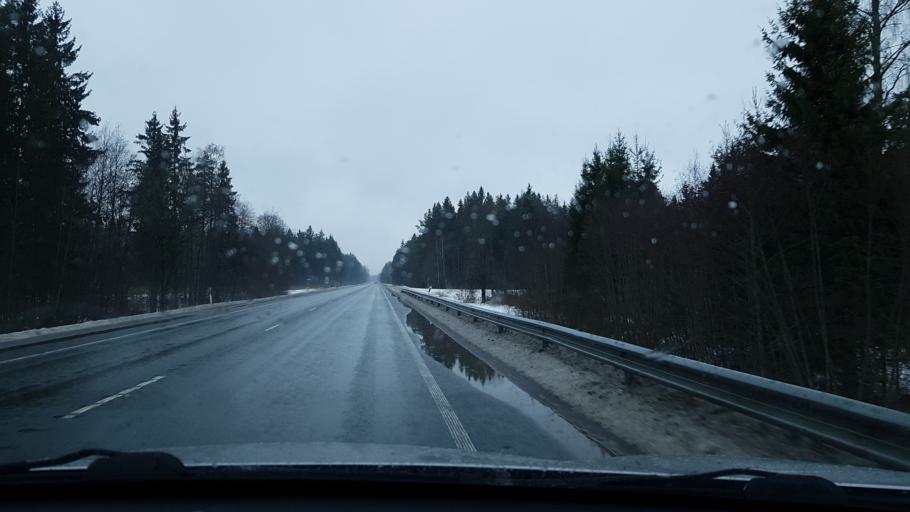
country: EE
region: Raplamaa
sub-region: Kohila vald
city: Kohila
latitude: 59.1434
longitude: 24.7881
